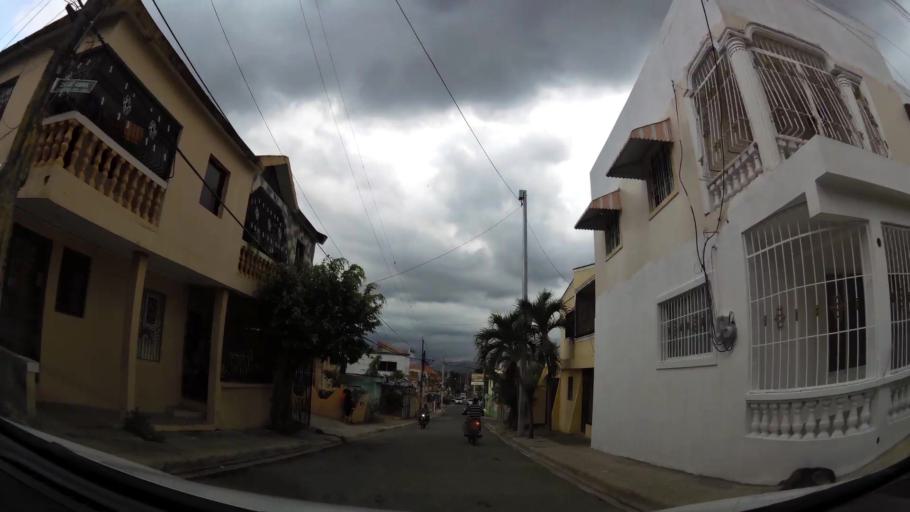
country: DO
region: San Cristobal
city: Villa Altagracia
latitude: 18.6657
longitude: -70.1702
